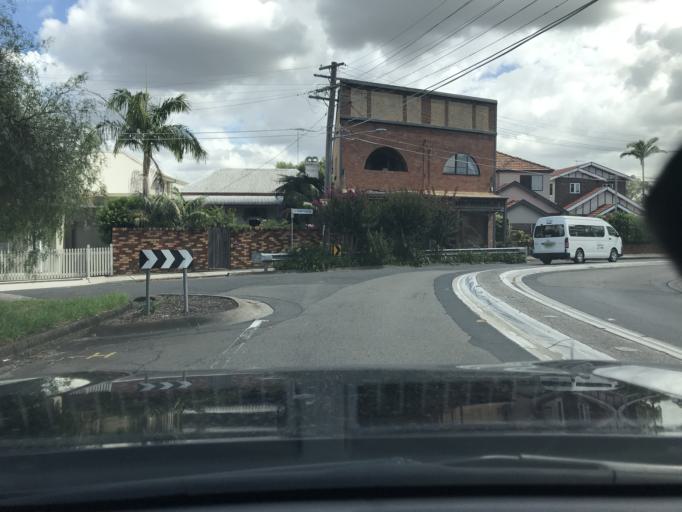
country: AU
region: New South Wales
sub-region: Canada Bay
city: Concord
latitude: -33.8455
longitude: 151.1070
